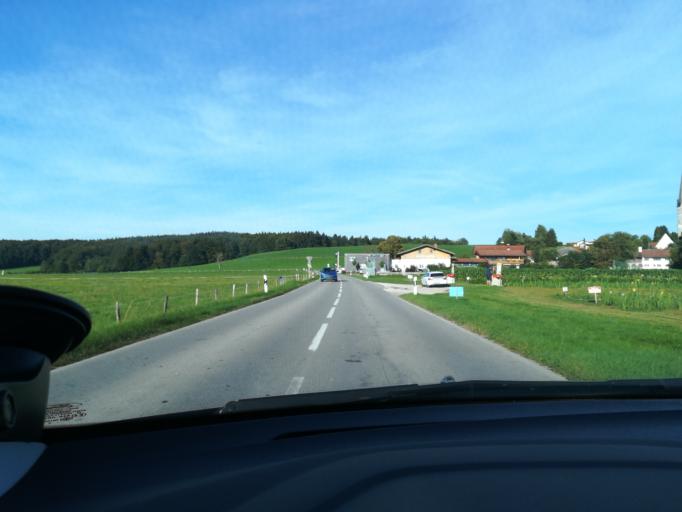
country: DE
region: Bavaria
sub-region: Upper Bavaria
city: Miesbach
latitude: 47.8223
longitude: 11.8337
